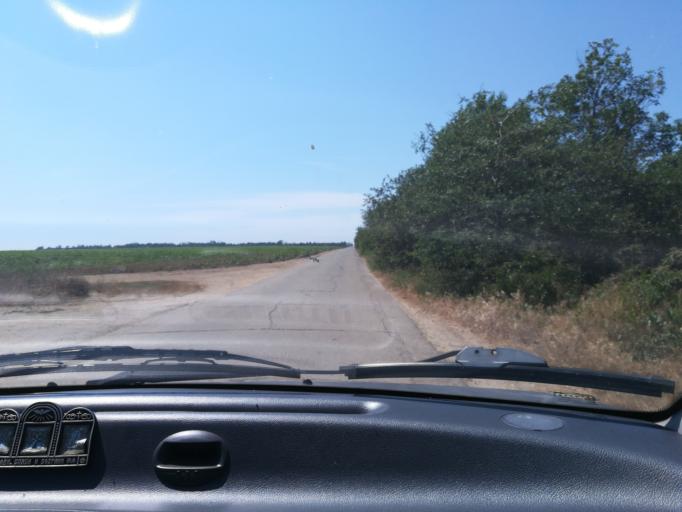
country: RU
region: Krasnodarskiy
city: Blagovetschenskaya
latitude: 45.0587
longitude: 37.1001
